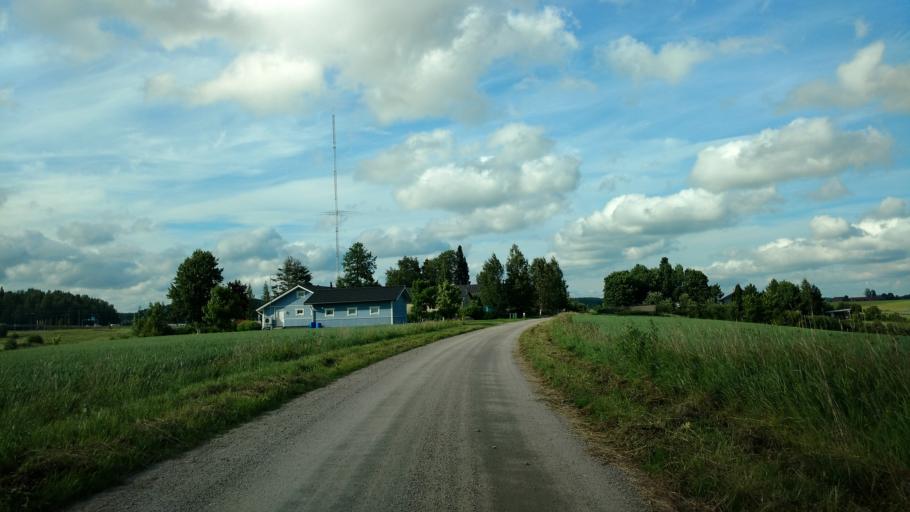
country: FI
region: Varsinais-Suomi
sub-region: Salo
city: Salo
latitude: 60.4123
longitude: 23.1686
